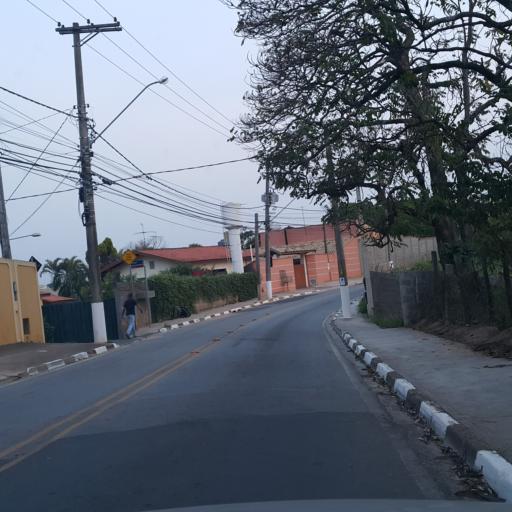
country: BR
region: Sao Paulo
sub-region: Vinhedo
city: Vinhedo
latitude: -23.0497
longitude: -46.9781
